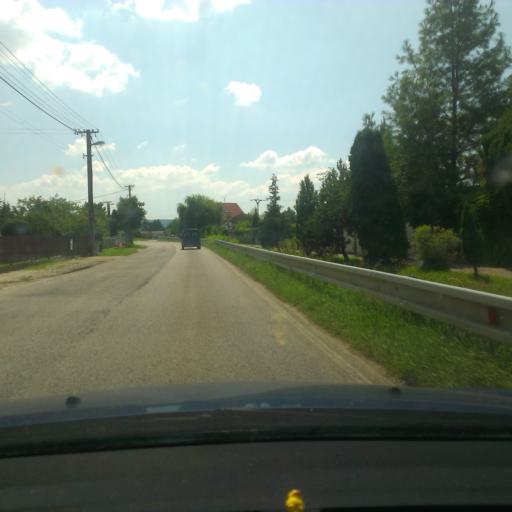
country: SK
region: Trnavsky
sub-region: Okres Trnava
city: Piestany
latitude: 48.5565
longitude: 17.8378
